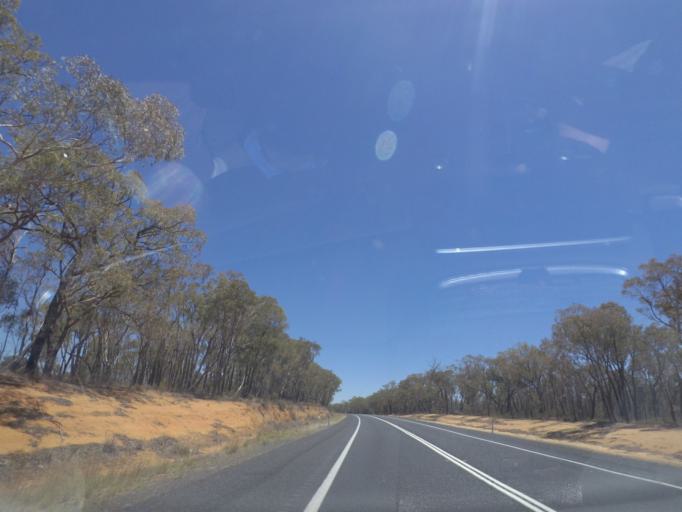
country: AU
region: New South Wales
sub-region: Warrumbungle Shire
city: Coonabarabran
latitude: -31.2047
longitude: 149.3356
